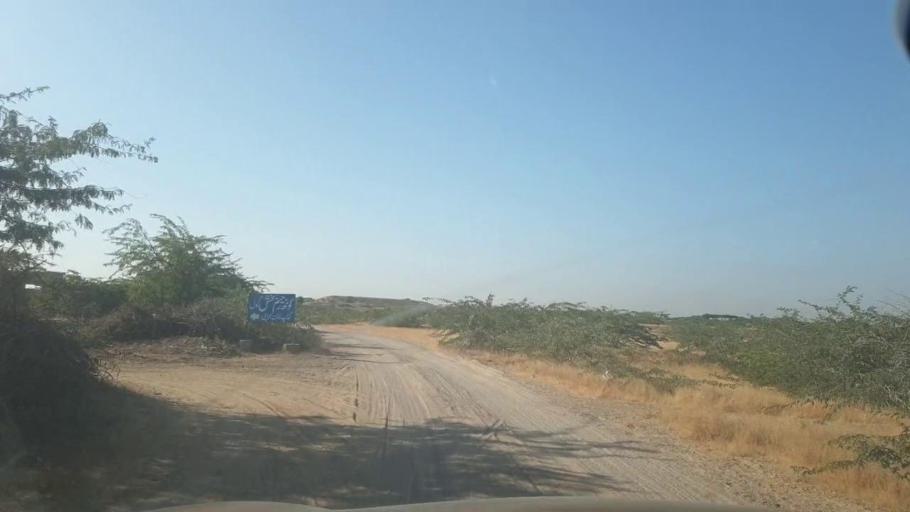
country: PK
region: Sindh
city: Malir Cantonment
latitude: 25.0382
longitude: 67.2609
